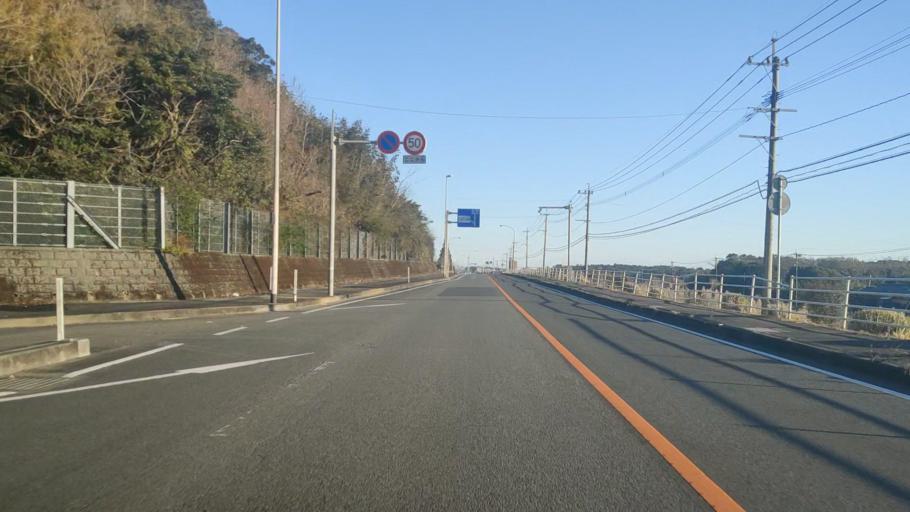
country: JP
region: Miyazaki
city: Takanabe
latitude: 32.1115
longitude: 131.5269
